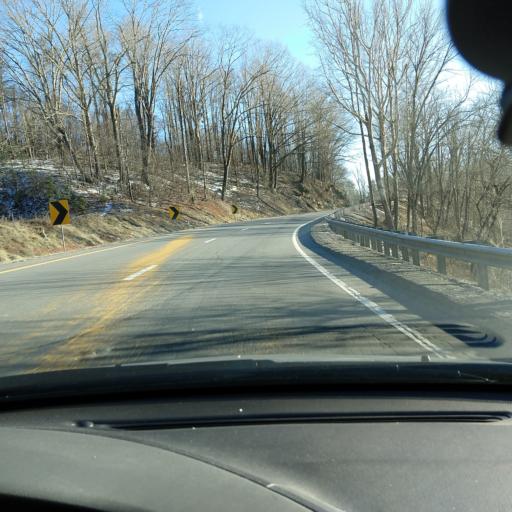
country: US
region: Virginia
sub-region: Botetourt County
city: Blue Ridge
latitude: 37.3683
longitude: -79.6945
